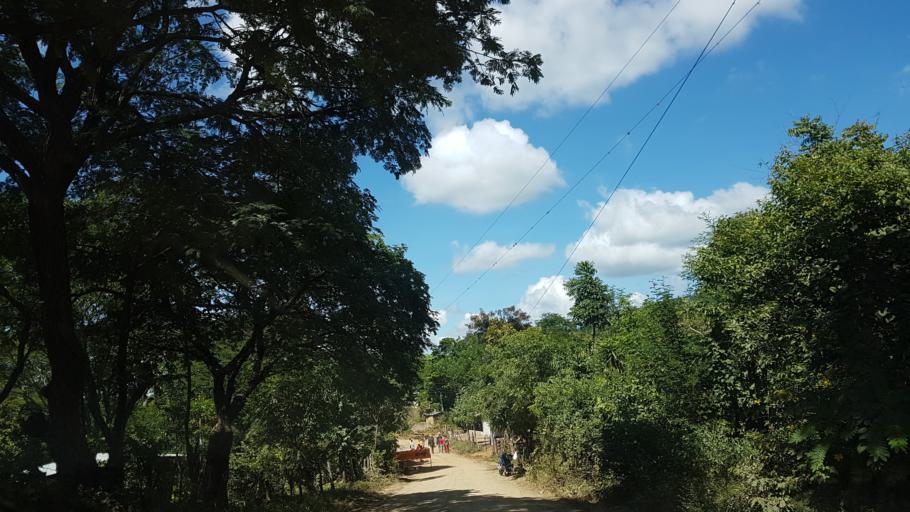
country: HN
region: El Paraiso
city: Santa Cruz
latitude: 13.7322
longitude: -86.6855
